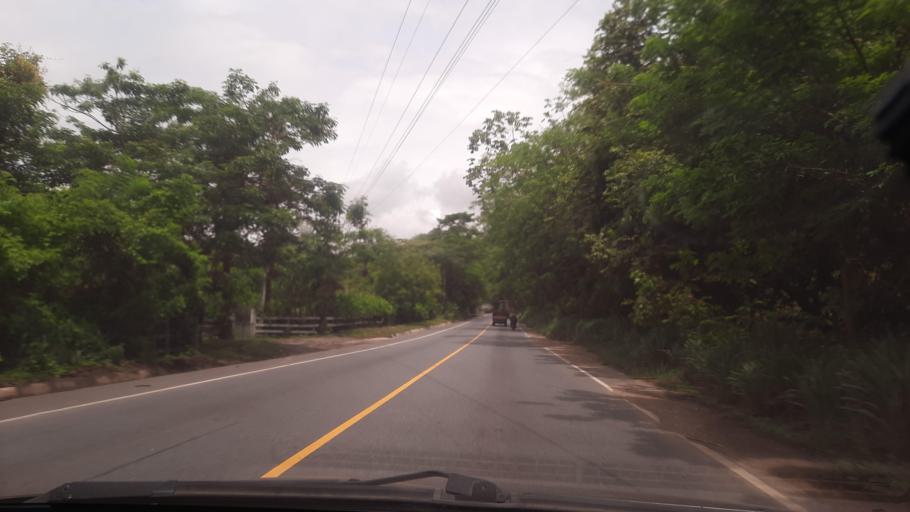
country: GT
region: Izabal
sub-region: Municipio de Los Amates
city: Los Amates
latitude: 15.2161
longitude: -89.2325
